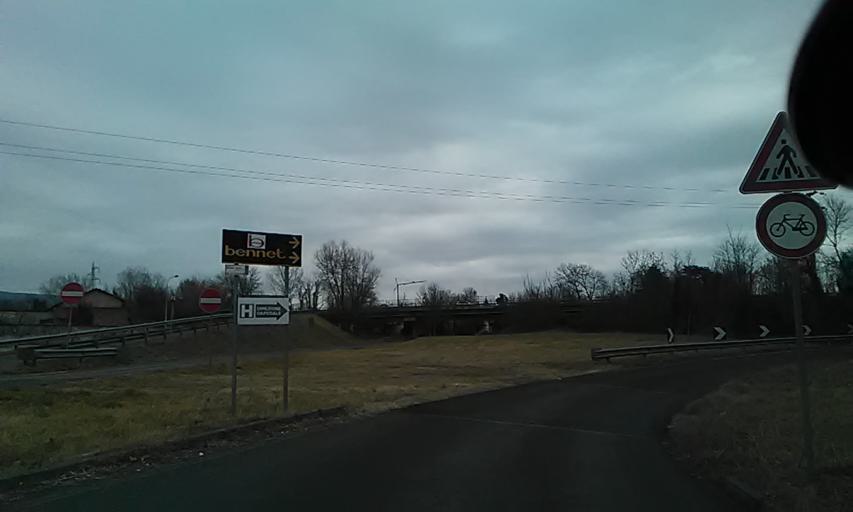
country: IT
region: Piedmont
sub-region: Provincia di Torino
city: Ivrea
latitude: 45.4651
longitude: 7.8864
